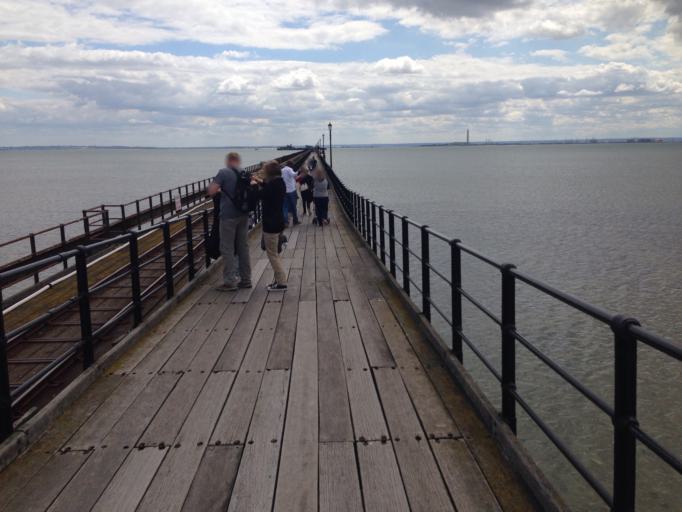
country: GB
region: England
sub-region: Southend-on-Sea
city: Southend-on-Sea
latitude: 51.5314
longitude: 0.7163
